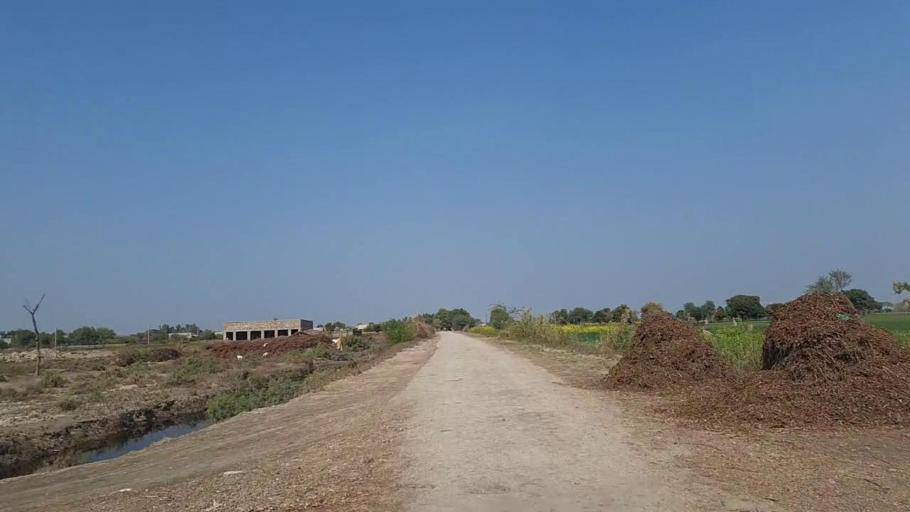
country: PK
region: Sindh
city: Nawabshah
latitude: 26.2883
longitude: 68.5138
